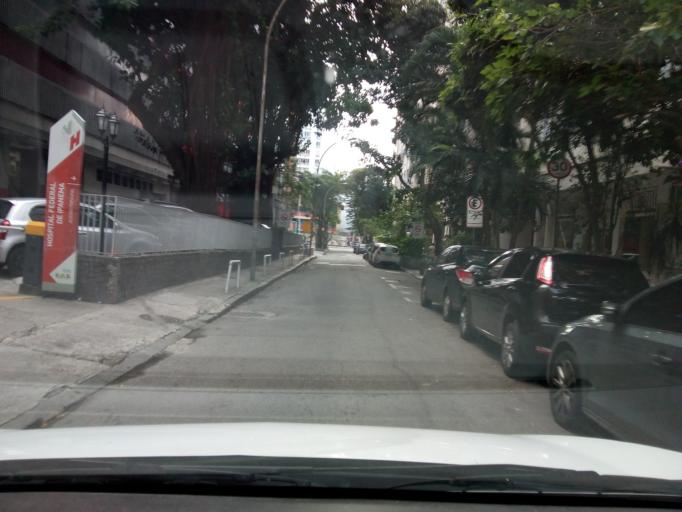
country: BR
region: Rio de Janeiro
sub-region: Rio De Janeiro
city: Rio de Janeiro
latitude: -22.9836
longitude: -43.1953
